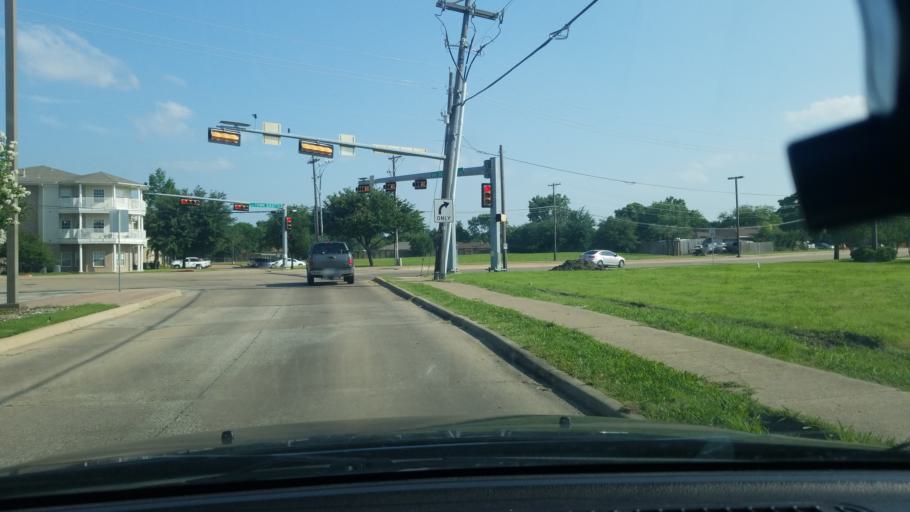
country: US
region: Texas
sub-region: Dallas County
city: Mesquite
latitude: 32.8138
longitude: -96.6074
